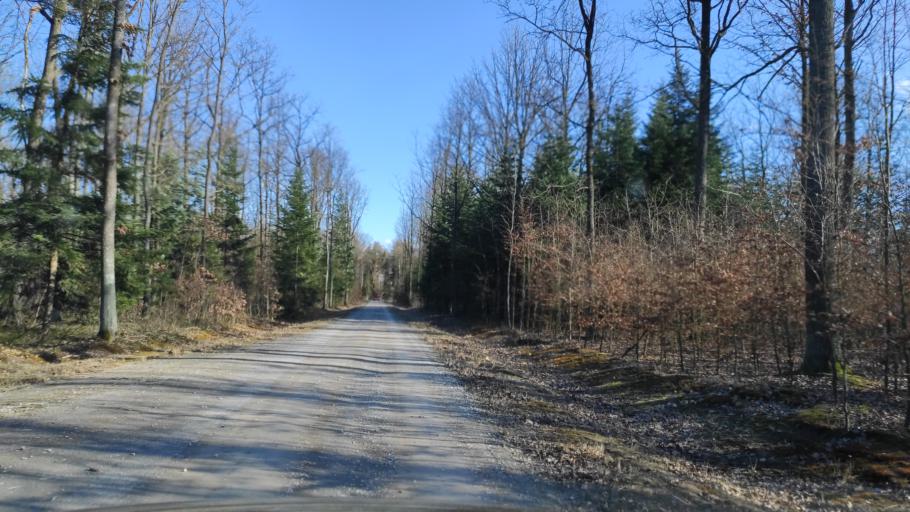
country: PL
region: Masovian Voivodeship
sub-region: Powiat radomski
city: Jedlnia-Letnisko
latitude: 51.4492
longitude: 21.2918
